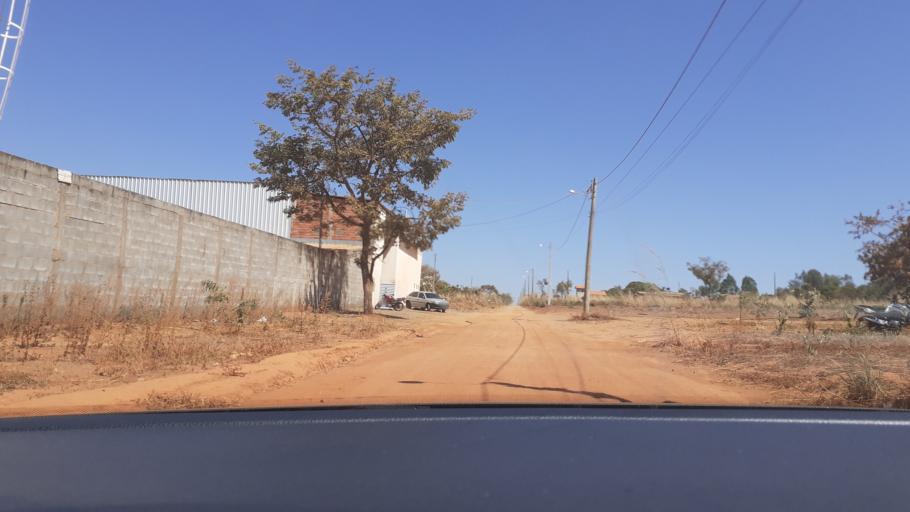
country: BR
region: Goias
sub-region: Aparecida De Goiania
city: Aparecida de Goiania
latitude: -16.8705
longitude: -49.2726
